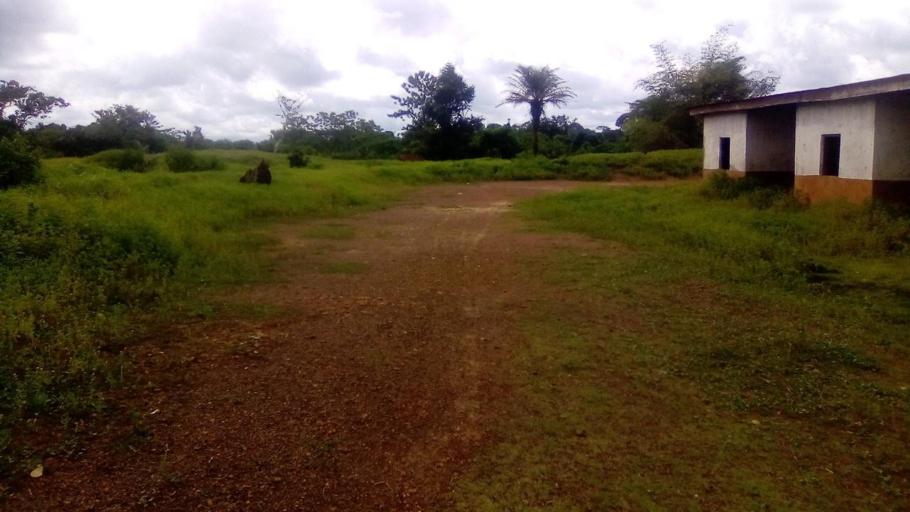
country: SL
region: Southern Province
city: Pujehun
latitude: 7.3728
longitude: -11.7249
